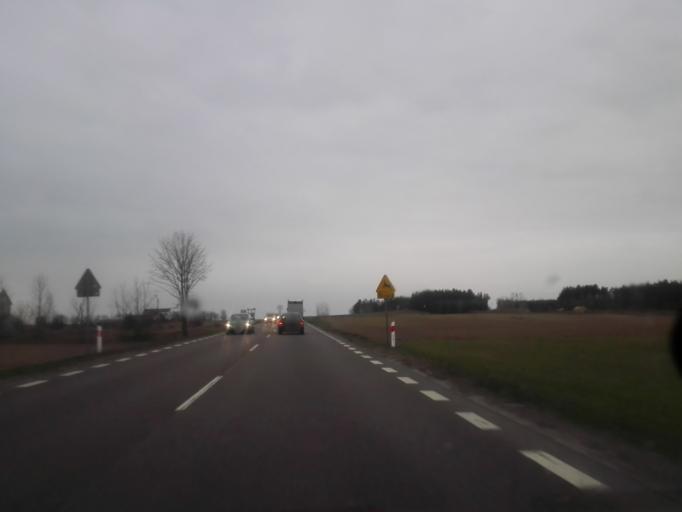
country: PL
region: Podlasie
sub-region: Powiat grajewski
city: Grajewo
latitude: 53.6177
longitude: 22.3914
